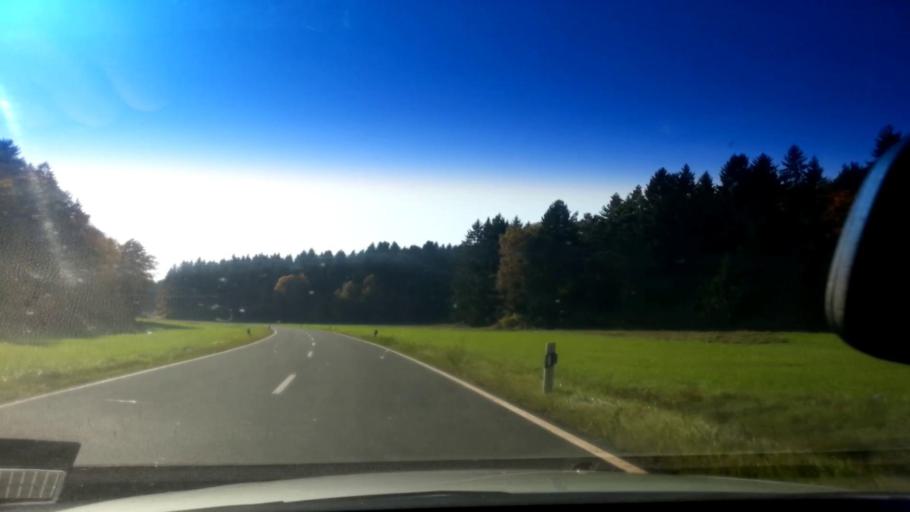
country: DE
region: Bavaria
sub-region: Upper Franconia
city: Poxdorf
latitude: 49.9833
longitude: 11.1310
